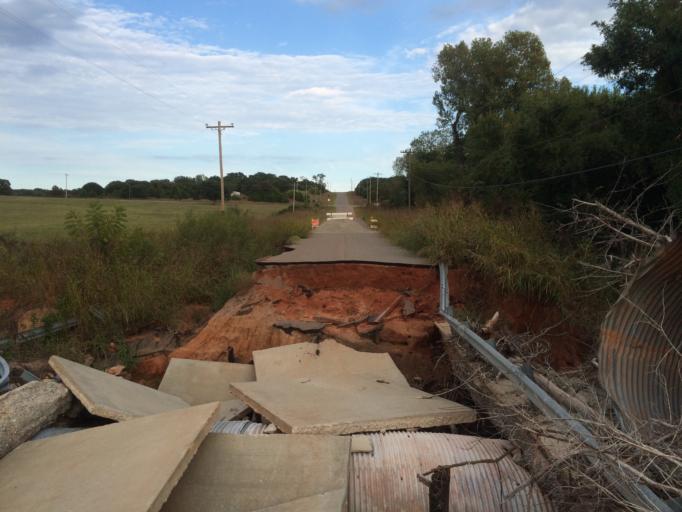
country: US
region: Oklahoma
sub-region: Cleveland County
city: Slaughterville
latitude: 35.1604
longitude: -97.2680
